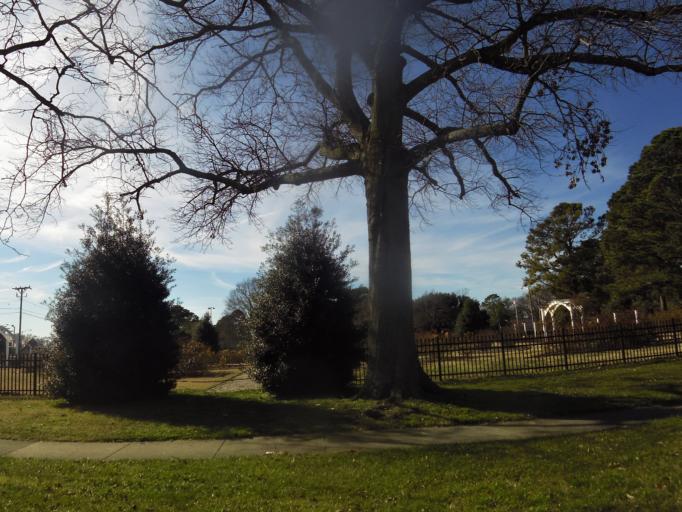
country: US
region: Virginia
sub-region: City of Newport News
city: Newport News
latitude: 37.0196
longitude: -76.4517
